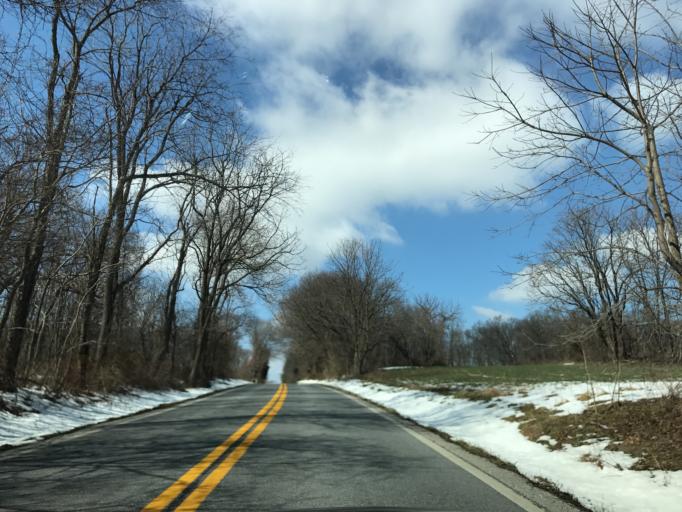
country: US
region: Maryland
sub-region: Carroll County
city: Hampstead
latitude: 39.6635
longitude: -76.8153
